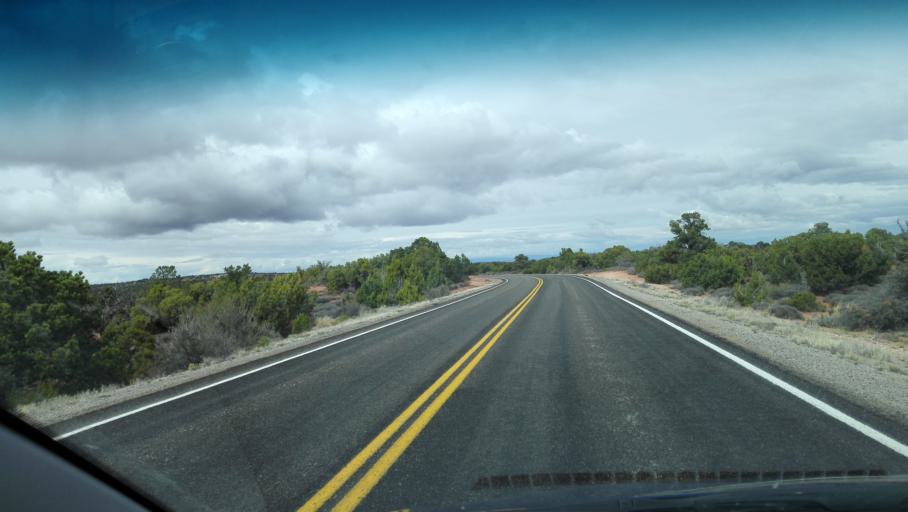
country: US
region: Utah
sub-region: Grand County
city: Moab
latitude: 38.3281
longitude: -109.8545
